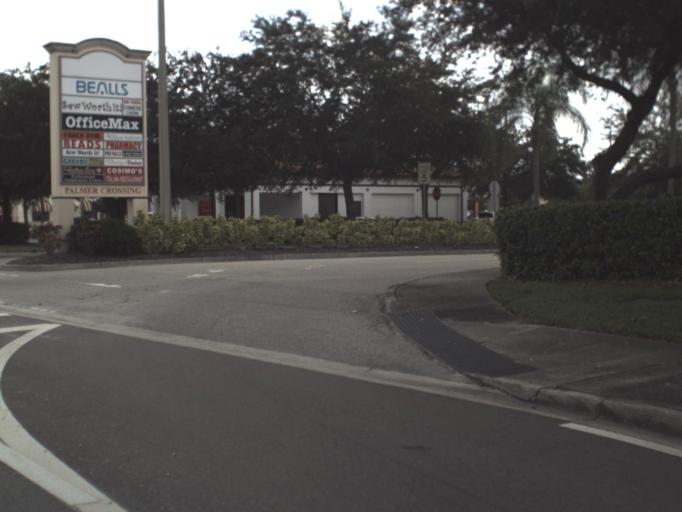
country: US
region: Florida
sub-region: Sarasota County
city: Bee Ridge
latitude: 27.2690
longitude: -82.4623
